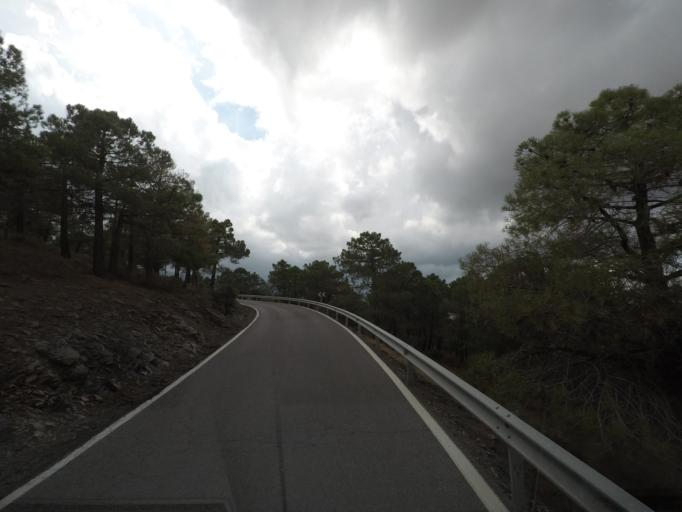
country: ES
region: Andalusia
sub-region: Provincia de Granada
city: Aldeire
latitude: 37.1624
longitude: -3.0550
